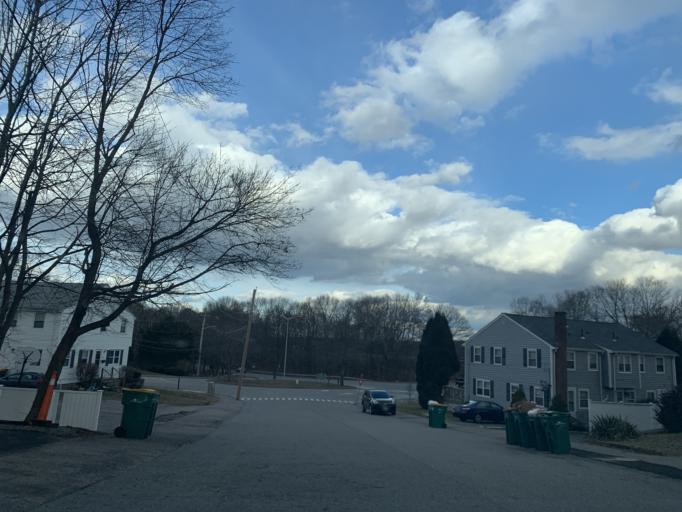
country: US
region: Massachusetts
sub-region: Norfolk County
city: Norwood
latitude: 42.2037
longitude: -71.1975
